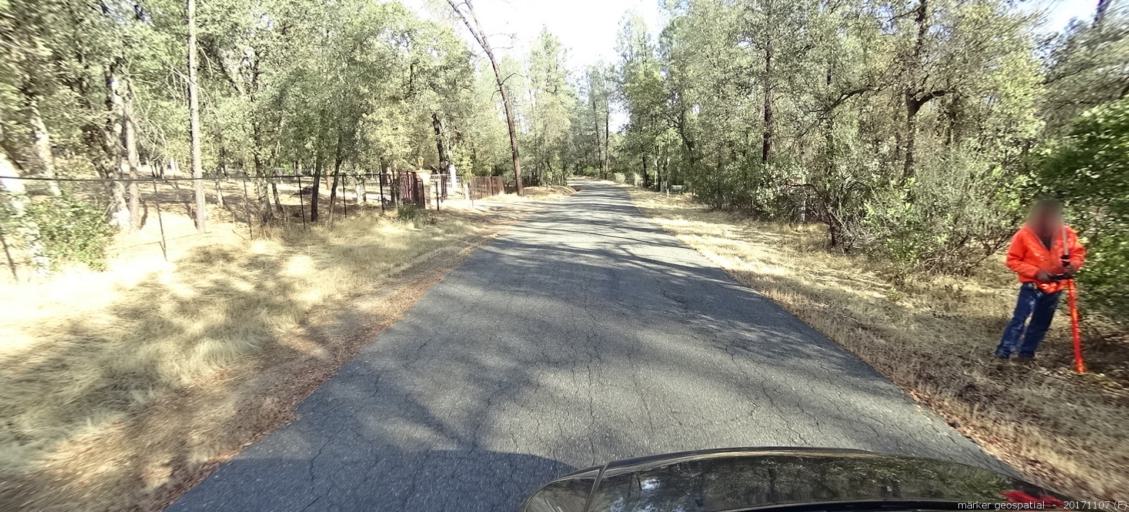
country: US
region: California
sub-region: Shasta County
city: Redding
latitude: 40.5495
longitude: -122.4469
